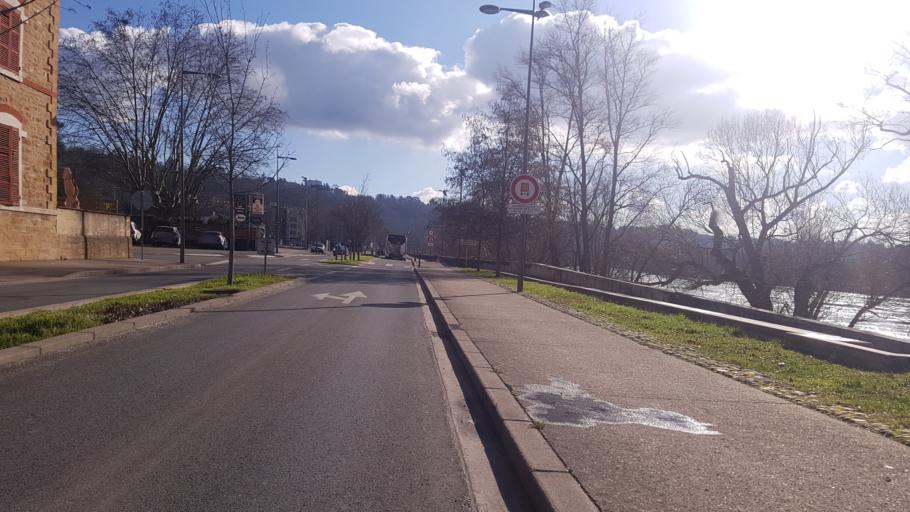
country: FR
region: Rhone-Alpes
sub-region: Departement du Rhone
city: Fontaines-sur-Saone
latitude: 45.8313
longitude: 4.8506
